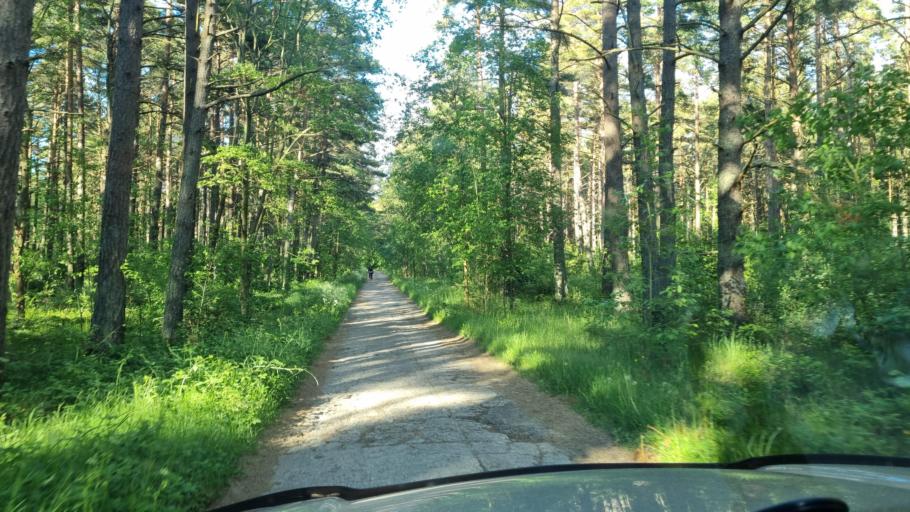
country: LV
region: Ventspils
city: Ventspils
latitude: 57.3720
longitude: 21.5220
